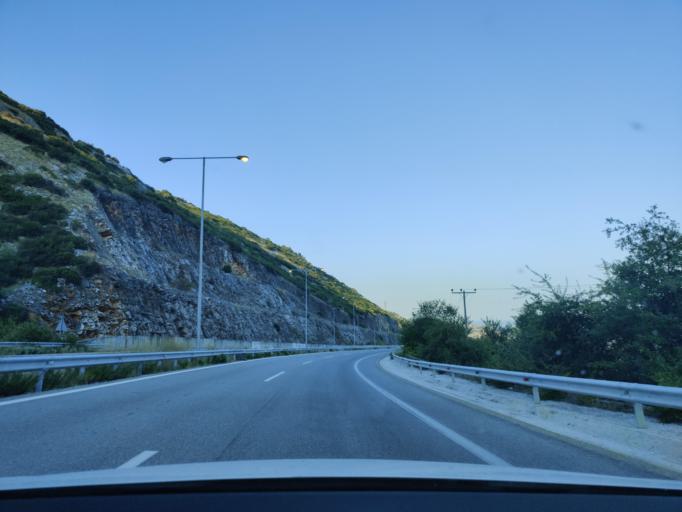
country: GR
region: East Macedonia and Thrace
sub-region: Nomos Kavalas
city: Kavala
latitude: 40.9621
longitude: 24.3983
